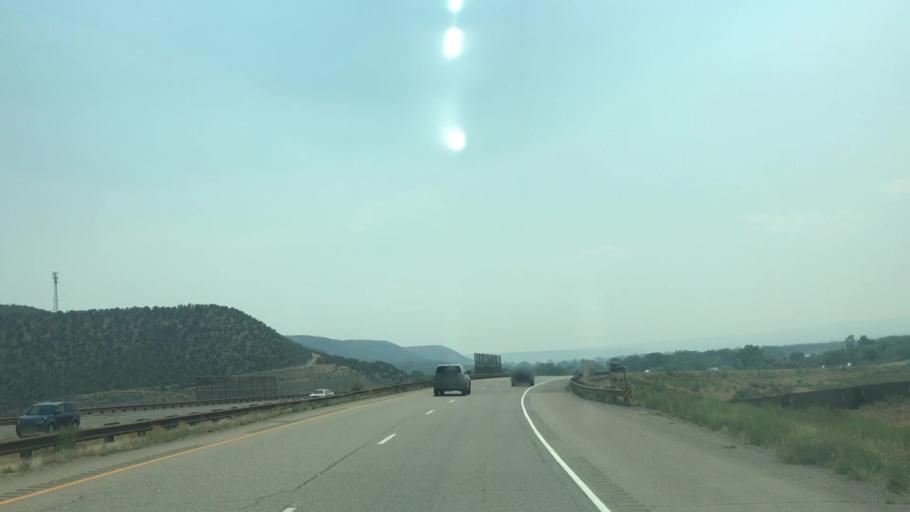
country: US
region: Colorado
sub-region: Garfield County
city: Parachute
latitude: 39.3560
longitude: -108.1711
